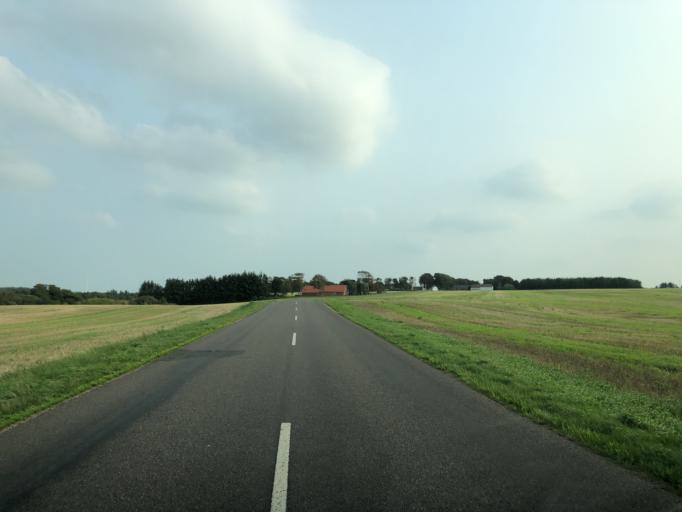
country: DK
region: Central Jutland
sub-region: Ringkobing-Skjern Kommune
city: Videbaek
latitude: 56.0480
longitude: 8.7052
